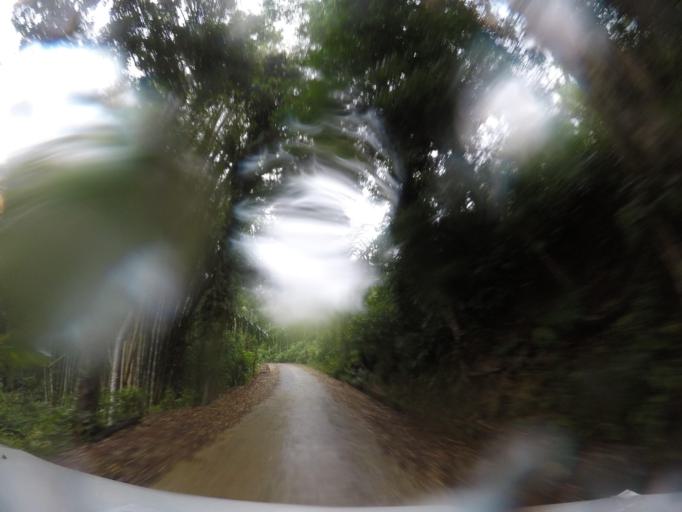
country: TL
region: Baucau
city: Venilale
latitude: -8.6321
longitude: 126.4271
